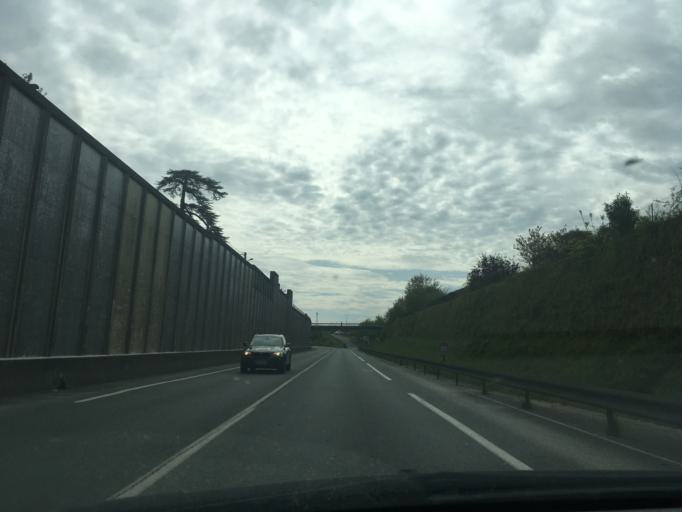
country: FR
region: Poitou-Charentes
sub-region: Departement de la Charente
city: Chateaubernard
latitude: 45.6827
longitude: -0.3385
